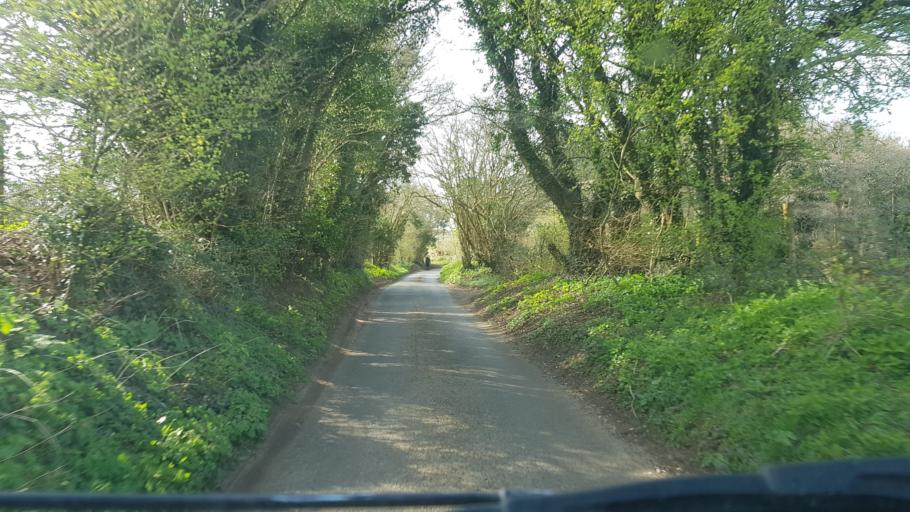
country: GB
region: England
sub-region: Surrey
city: Chilworth
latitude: 51.2231
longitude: -0.5076
